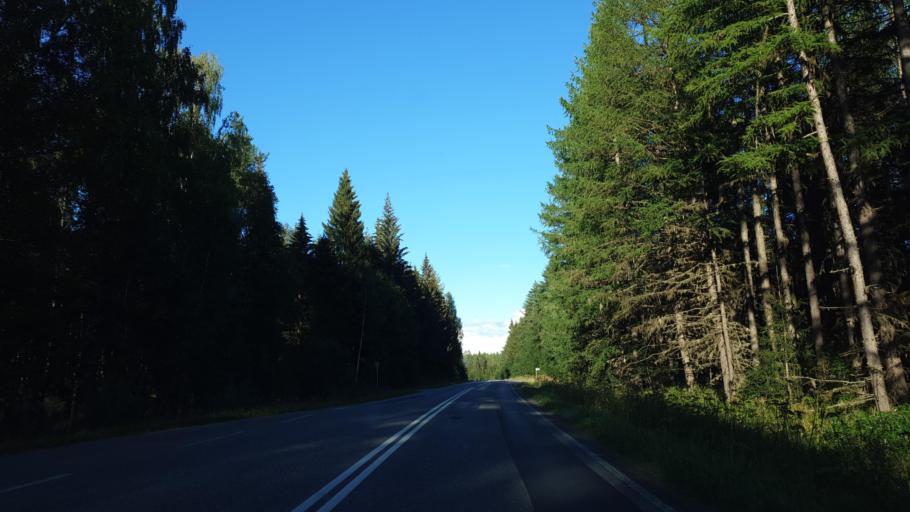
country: FI
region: Northern Savo
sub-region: Koillis-Savo
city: Juankoski
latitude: 63.0901
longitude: 28.4031
